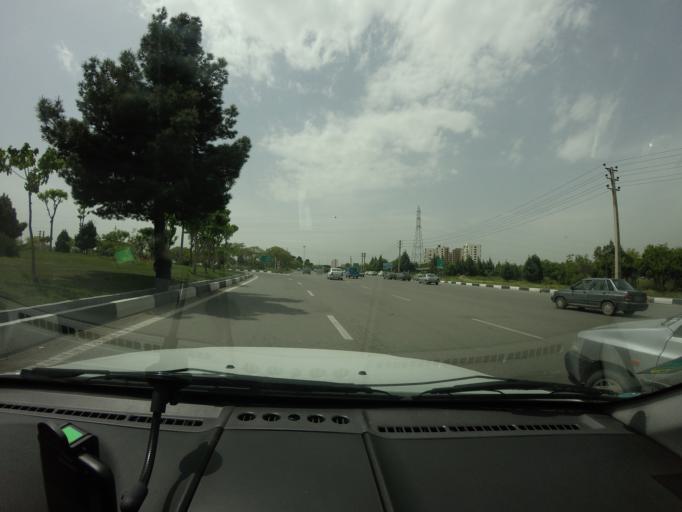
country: IR
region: Tehran
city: Eslamshahr
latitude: 35.5169
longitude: 51.2289
